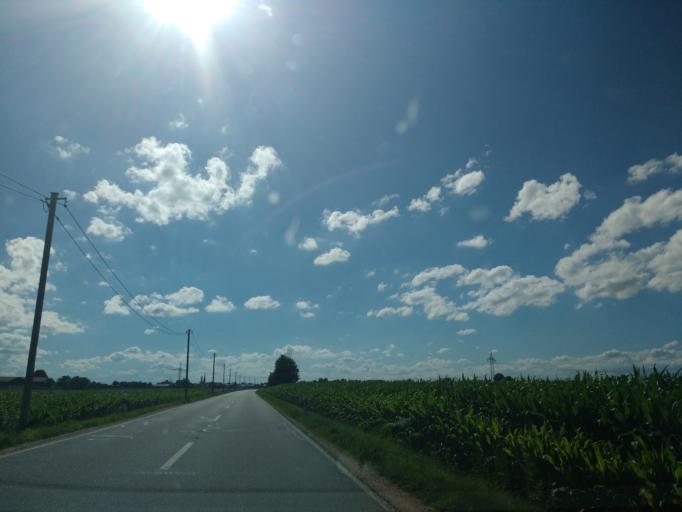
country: DE
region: Bavaria
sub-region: Upper Bavaria
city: Unterneukirchen
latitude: 48.1669
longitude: 12.6417
